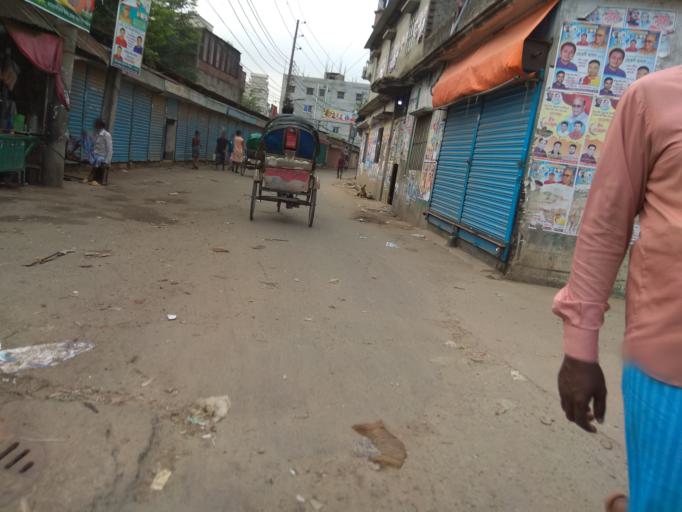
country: BD
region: Dhaka
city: Azimpur
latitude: 23.7133
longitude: 90.3785
